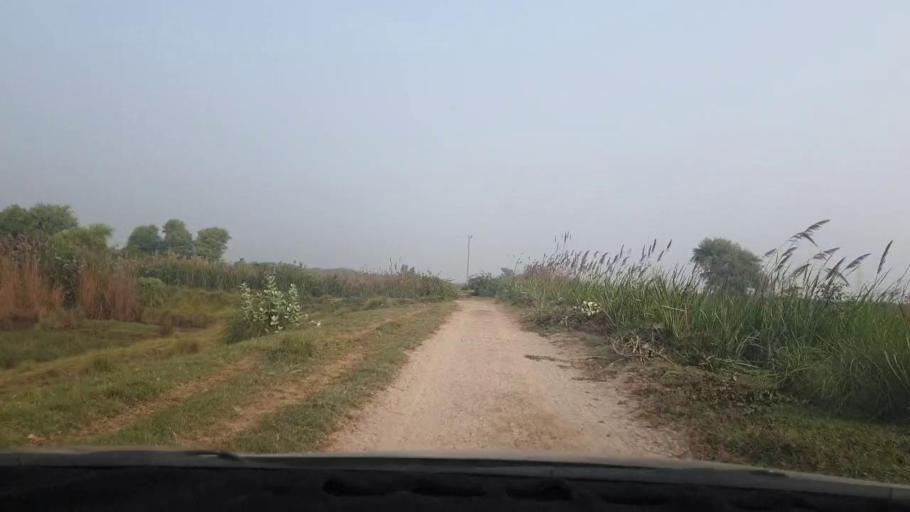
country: PK
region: Sindh
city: Matiari
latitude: 25.6005
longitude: 68.5511
